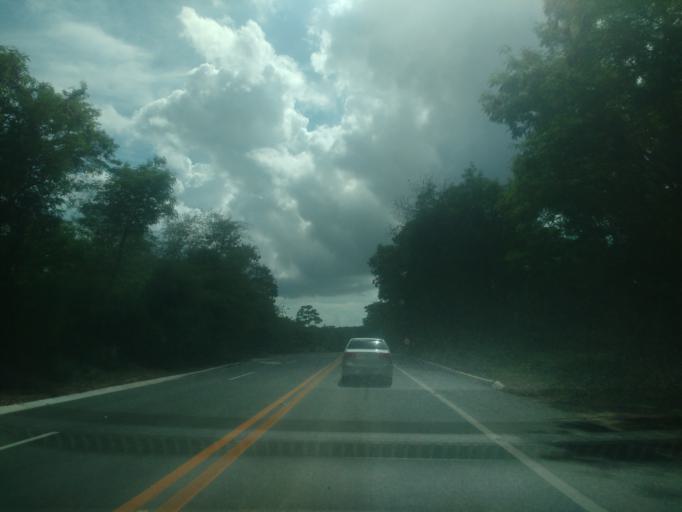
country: BR
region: Alagoas
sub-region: Marechal Deodoro
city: Marechal Deodoro
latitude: -9.6863
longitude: -35.8243
